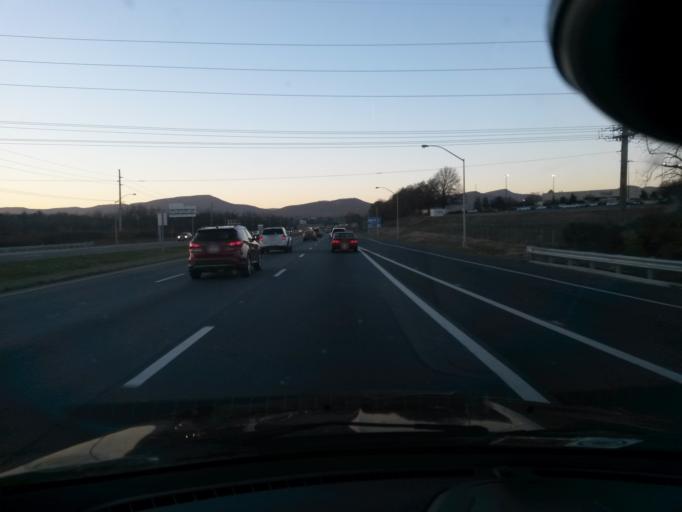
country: US
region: Virginia
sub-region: City of Roanoke
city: Roanoke
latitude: 37.3001
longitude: -79.9625
